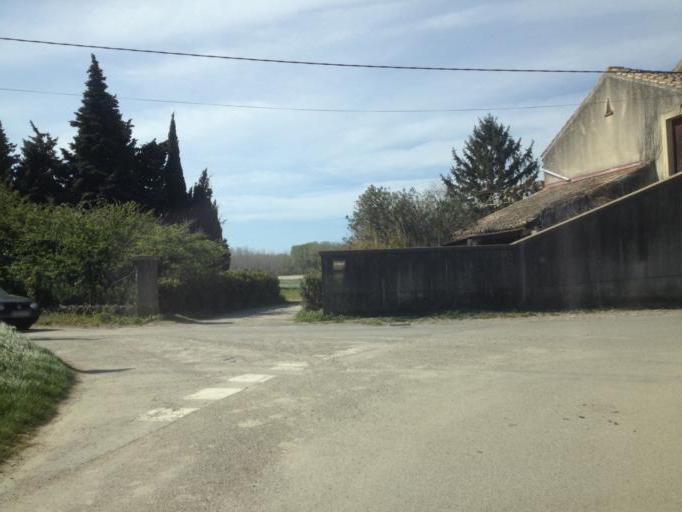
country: FR
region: Provence-Alpes-Cote d'Azur
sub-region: Departement du Vaucluse
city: Caderousse
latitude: 44.1018
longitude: 4.7353
